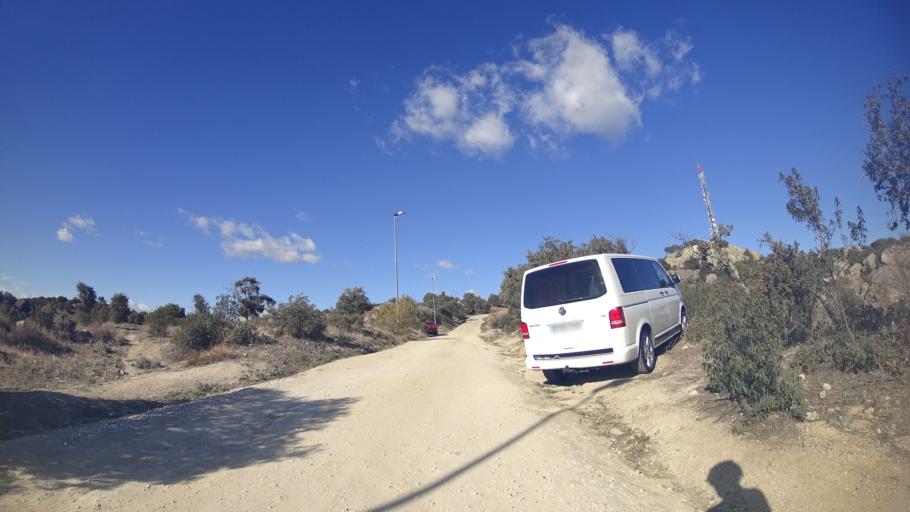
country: ES
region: Madrid
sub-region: Provincia de Madrid
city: Torrelodones
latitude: 40.5804
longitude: -3.9396
